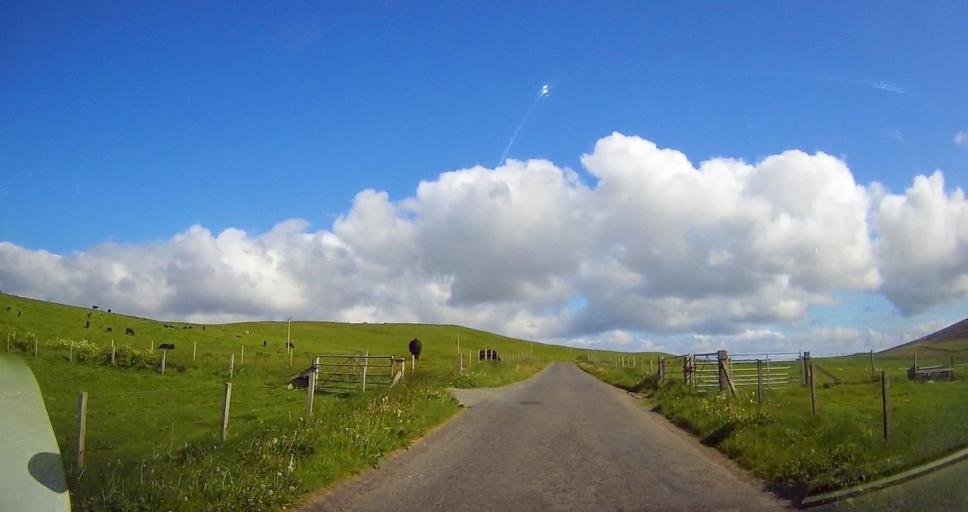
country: GB
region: Scotland
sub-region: Orkney Islands
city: Stromness
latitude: 58.9818
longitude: -3.1391
